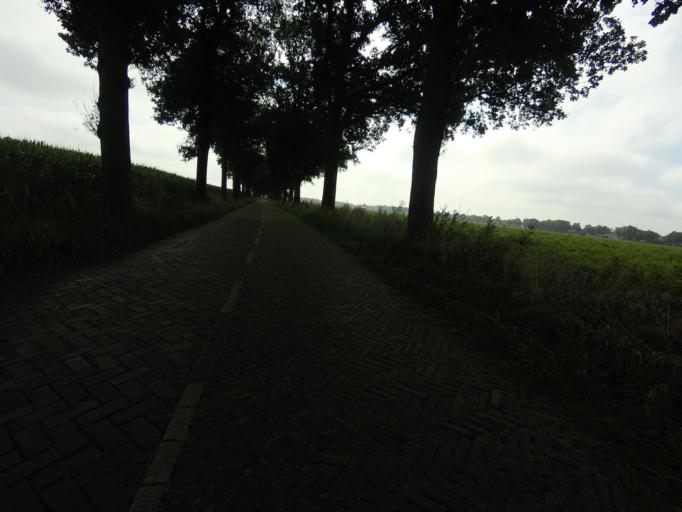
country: NL
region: Drenthe
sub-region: Gemeente Tynaarlo
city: Vries
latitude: 53.1056
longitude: 6.5379
